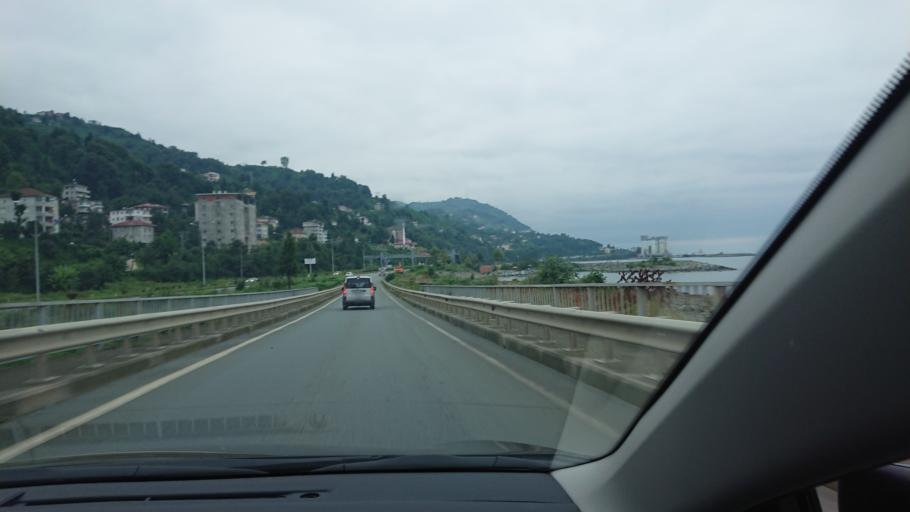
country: TR
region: Rize
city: Cayeli
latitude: 41.0813
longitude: 40.7019
